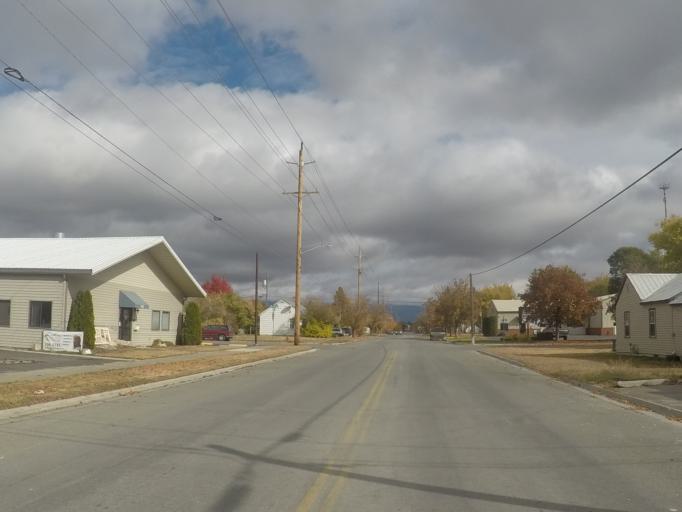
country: US
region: Montana
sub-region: Flathead County
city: Kalispell
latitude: 48.1991
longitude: -114.3215
